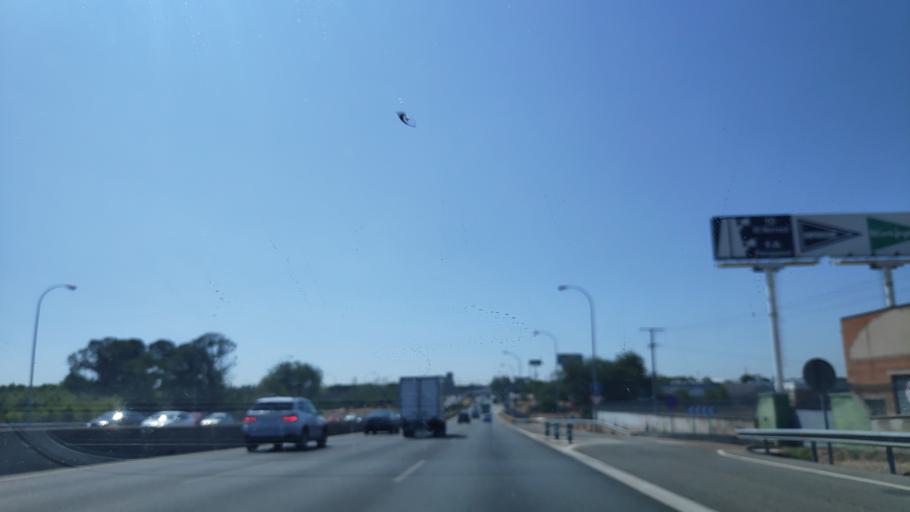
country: ES
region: Madrid
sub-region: Provincia de Madrid
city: Villaverde
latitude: 40.3548
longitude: -3.7222
